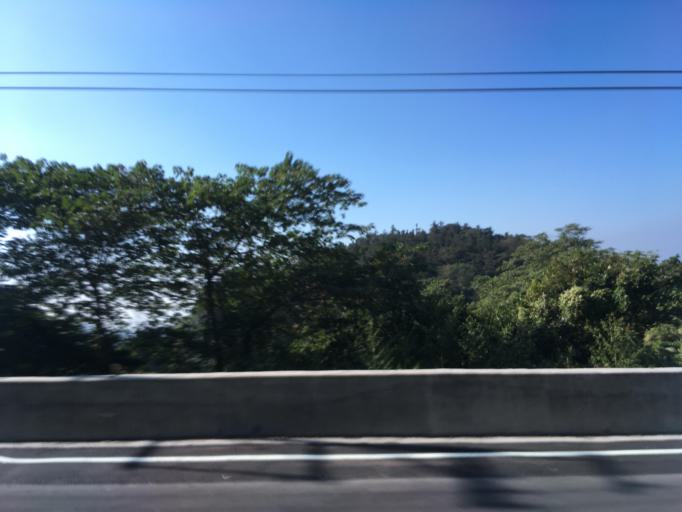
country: TW
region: Taiwan
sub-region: Chiayi
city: Jiayi Shi
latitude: 23.4156
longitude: 120.6448
